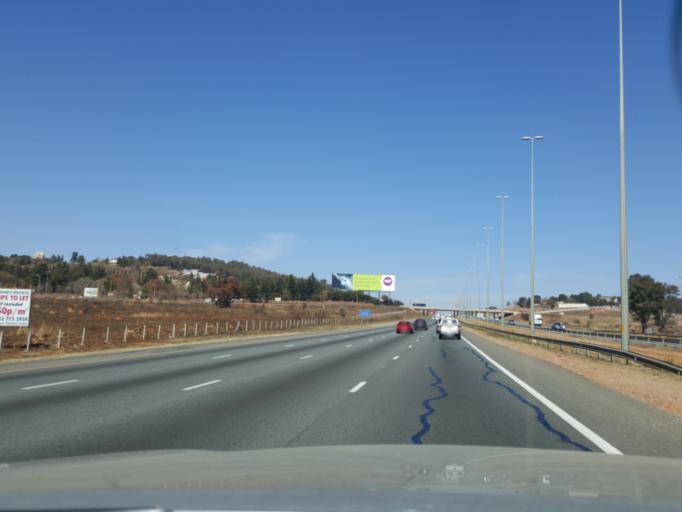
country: ZA
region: Gauteng
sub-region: City of Tshwane Metropolitan Municipality
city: Centurion
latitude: -25.8818
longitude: 28.2549
